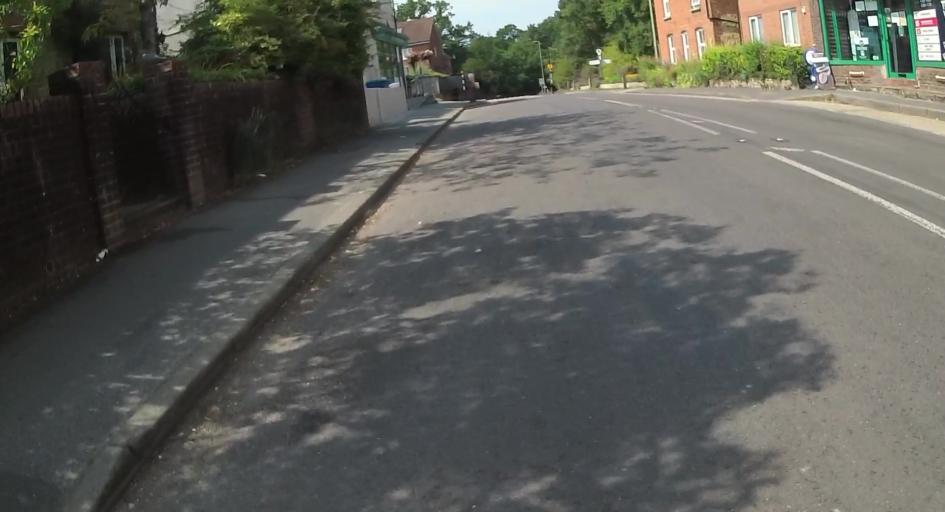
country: GB
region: England
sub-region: Surrey
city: Farnham
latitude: 51.1963
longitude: -0.7900
